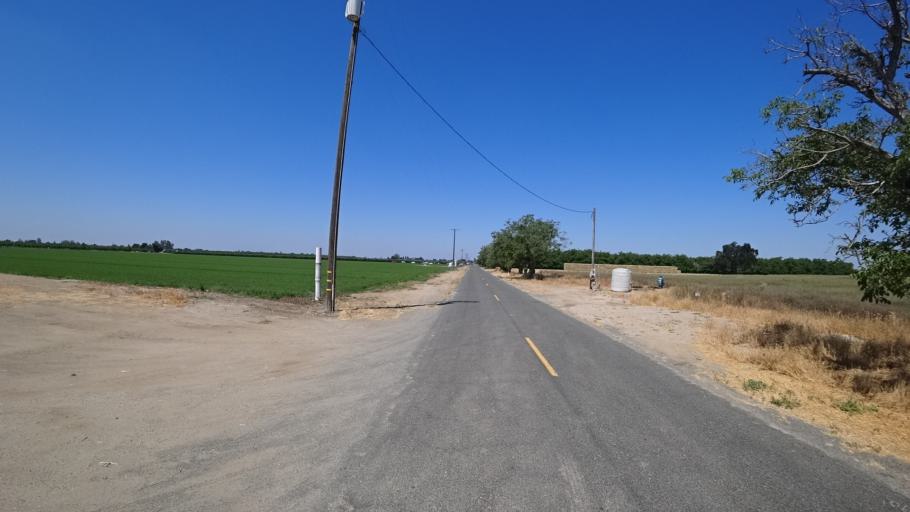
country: US
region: California
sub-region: Fresno County
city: Laton
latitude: 36.4380
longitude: -119.6142
